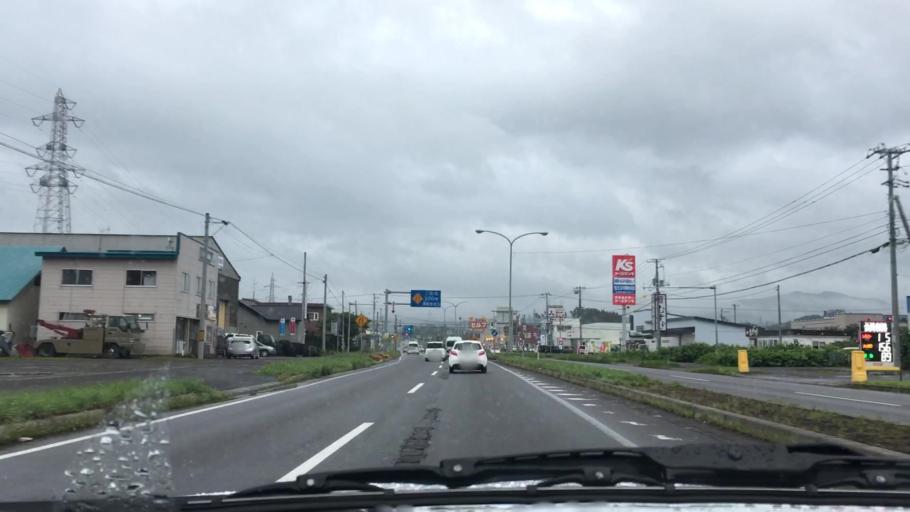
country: JP
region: Hokkaido
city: Nanae
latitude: 42.2503
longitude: 140.2858
